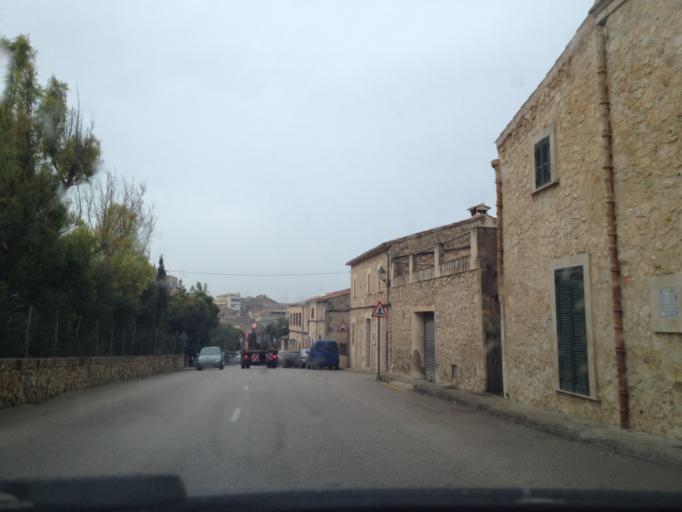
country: ES
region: Balearic Islands
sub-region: Illes Balears
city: Sineu
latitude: 39.6467
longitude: 3.0156
